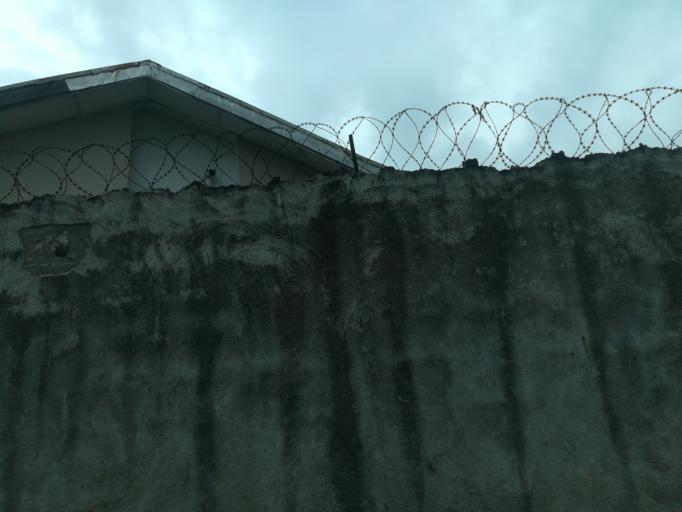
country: NG
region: Rivers
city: Port Harcourt
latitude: 4.8195
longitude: 7.0181
